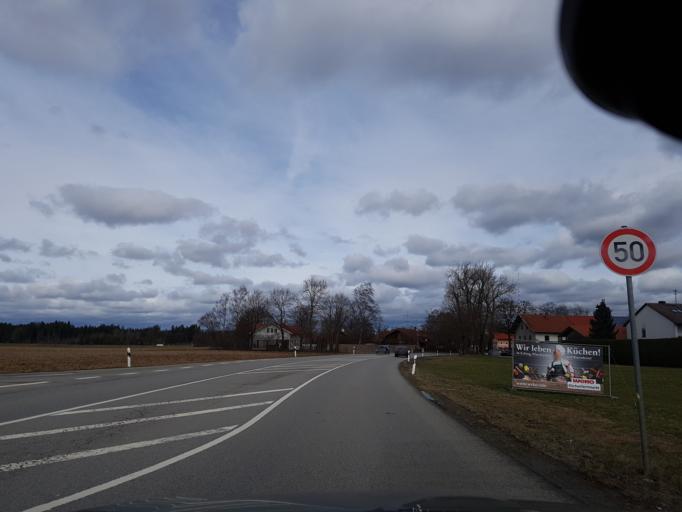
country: DE
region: Bavaria
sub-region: Upper Bavaria
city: Hohenkirchen-Siegertsbrunn
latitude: 47.9912
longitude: 11.7342
